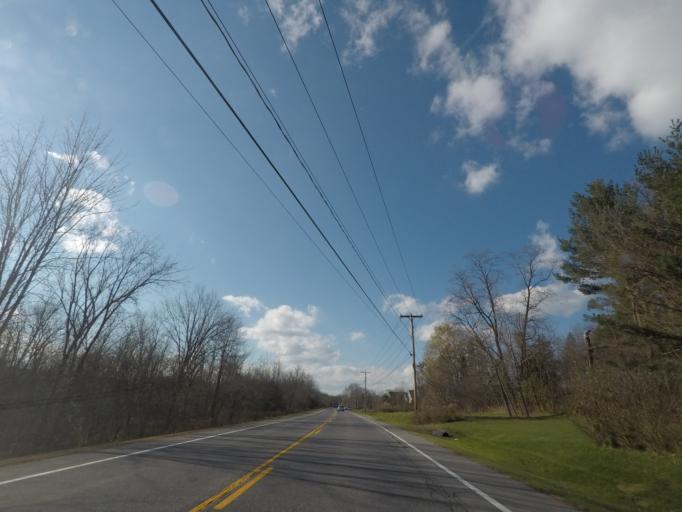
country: US
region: New York
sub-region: Saratoga County
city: Country Knolls
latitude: 42.8921
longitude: -73.8343
